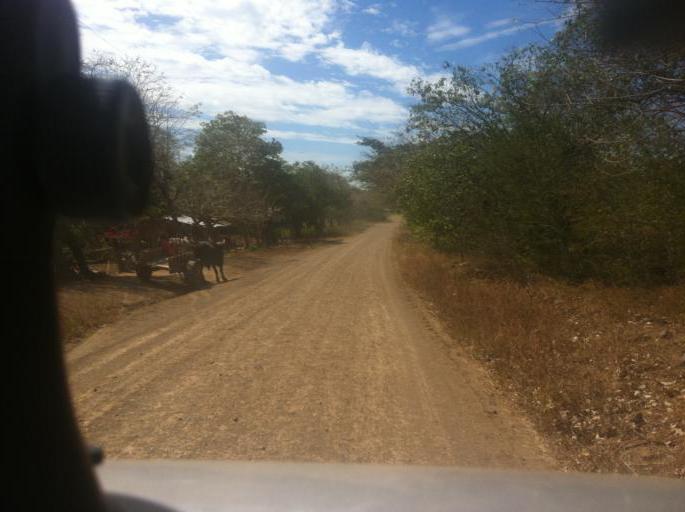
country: NI
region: Rivas
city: Tola
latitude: 11.5465
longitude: -86.0410
